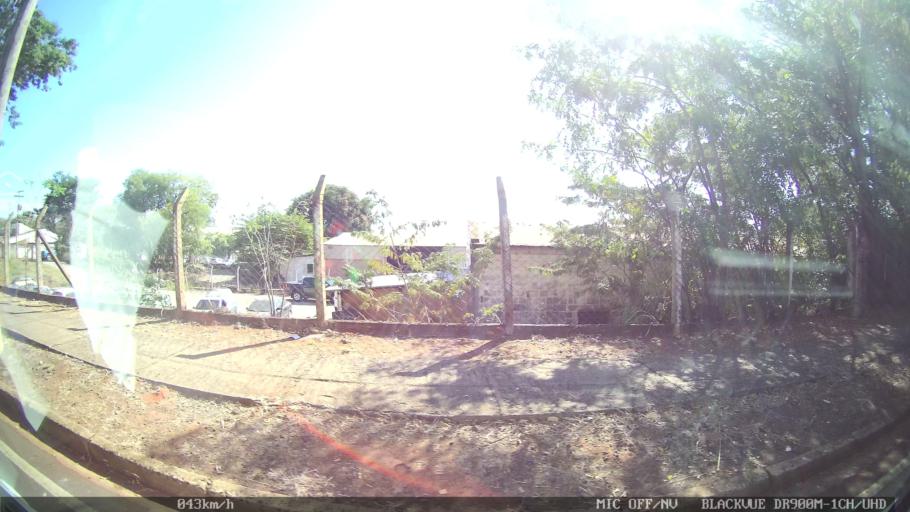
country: BR
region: Sao Paulo
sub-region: Sao Jose Do Rio Preto
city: Sao Jose do Rio Preto
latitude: -20.8116
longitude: -49.4221
